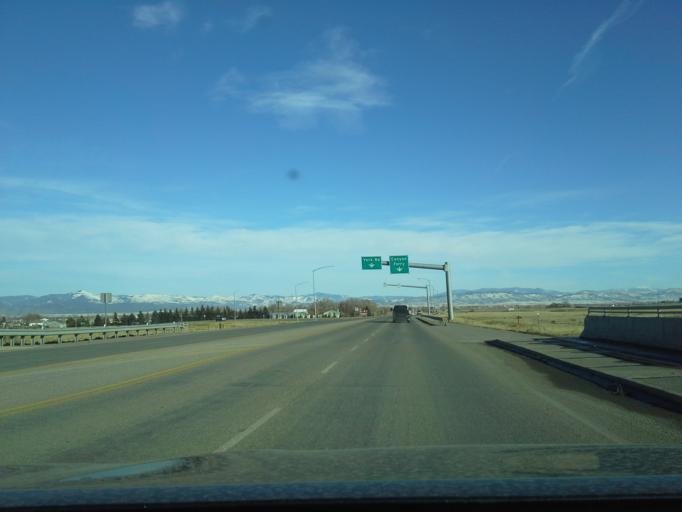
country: US
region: Montana
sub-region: Lewis and Clark County
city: Helena
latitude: 46.6167
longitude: -111.9940
